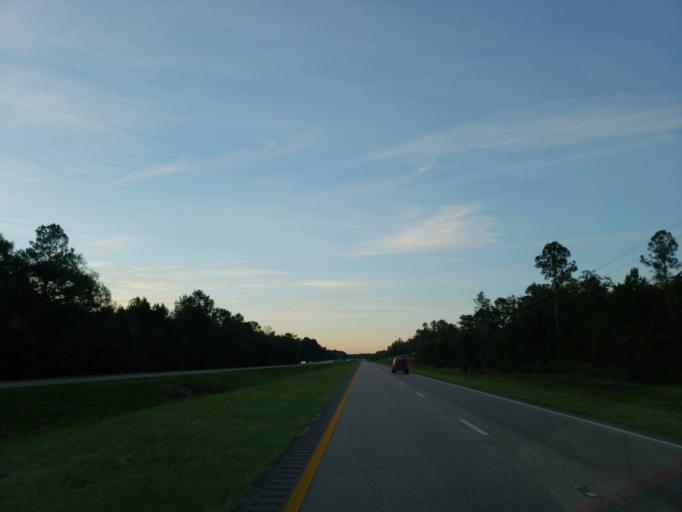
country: US
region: Mississippi
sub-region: Wayne County
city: Belmont
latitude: 31.5865
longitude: -88.5461
